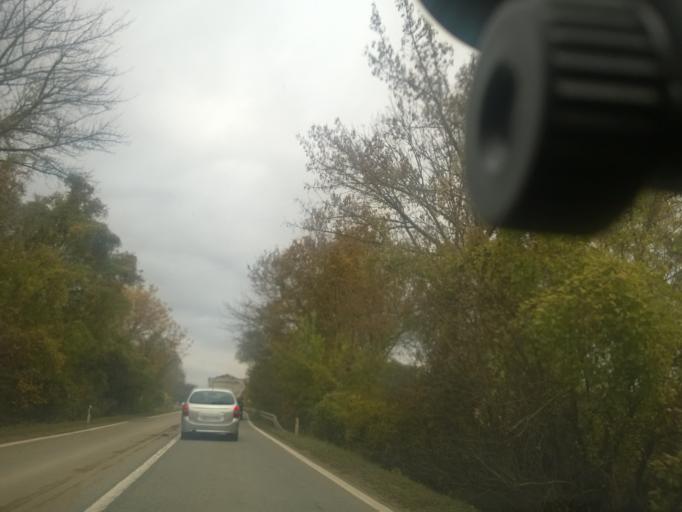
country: RS
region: Central Serbia
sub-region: Pirotski Okrug
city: Dimitrovgrad
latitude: 43.0646
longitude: 22.6792
